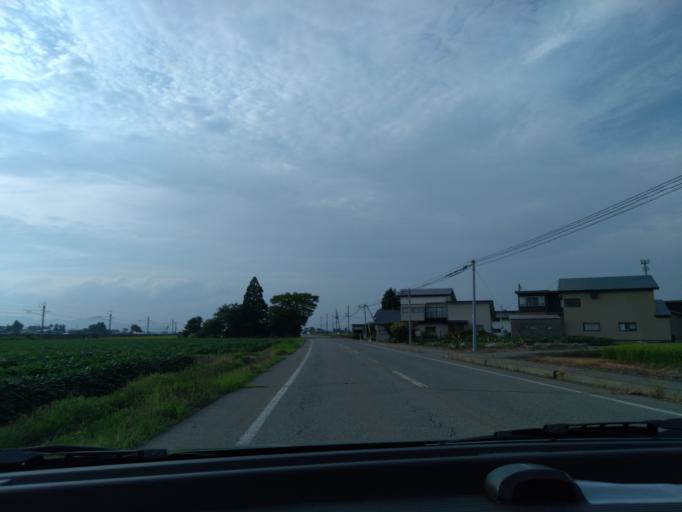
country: JP
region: Akita
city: Omagari
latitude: 39.3907
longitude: 140.5250
